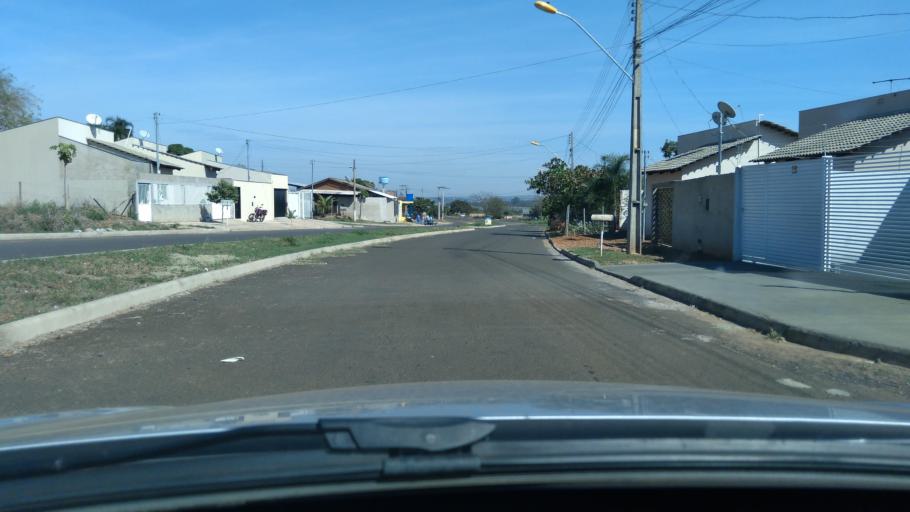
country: BR
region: Goias
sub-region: Mineiros
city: Mineiros
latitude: -17.5800
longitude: -52.5599
